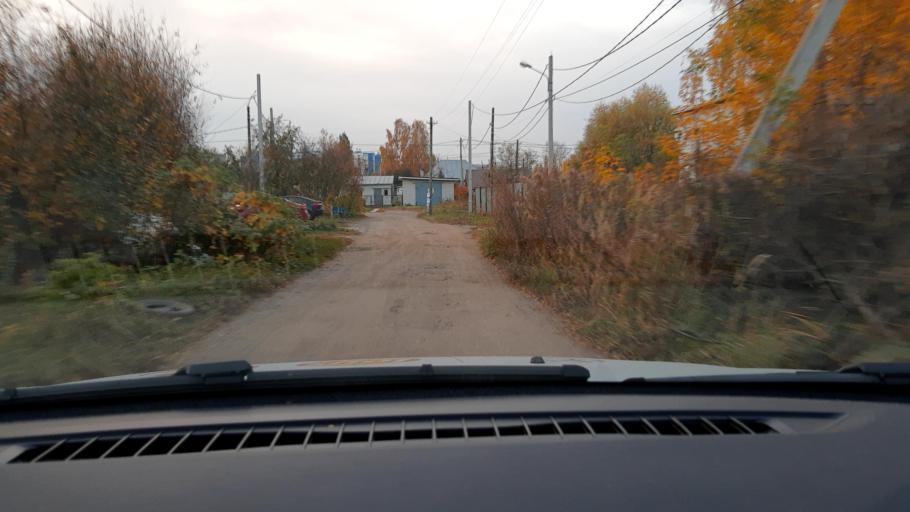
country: RU
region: Nizjnij Novgorod
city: Burevestnik
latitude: 56.2114
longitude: 43.8155
